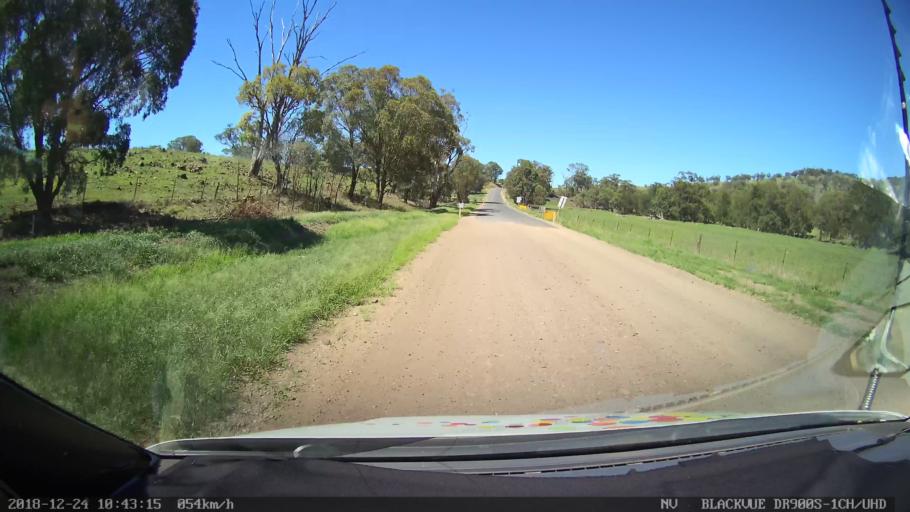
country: AU
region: New South Wales
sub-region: Upper Hunter Shire
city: Merriwa
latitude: -31.8814
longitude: 150.4474
